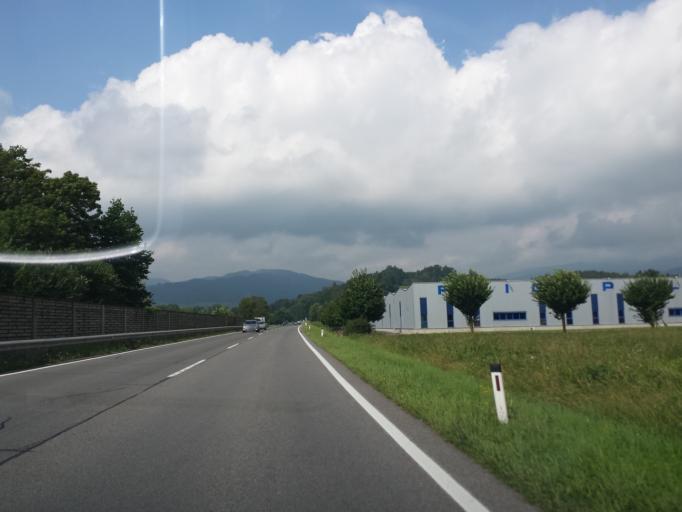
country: AT
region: Styria
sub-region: Politischer Bezirk Deutschlandsberg
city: Rassach
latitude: 46.8309
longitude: 15.2538
